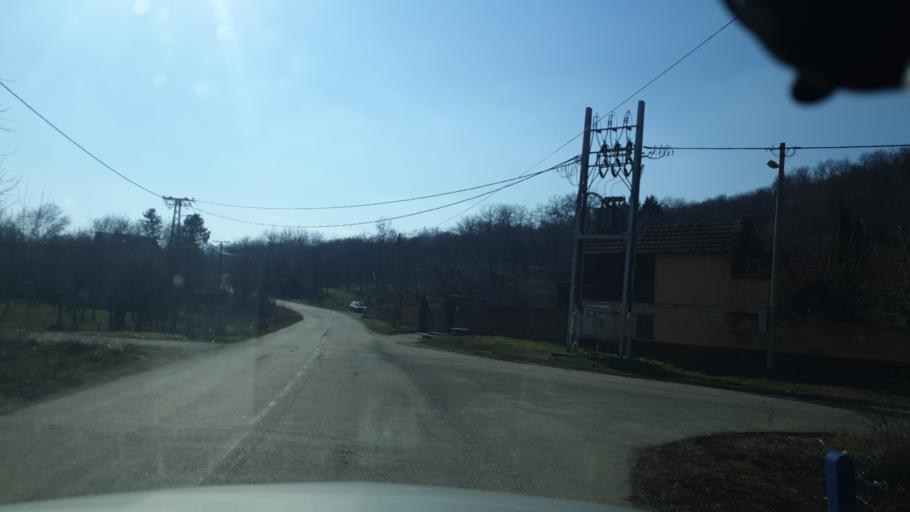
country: RS
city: Vrdnik
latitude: 45.1107
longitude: 19.7668
